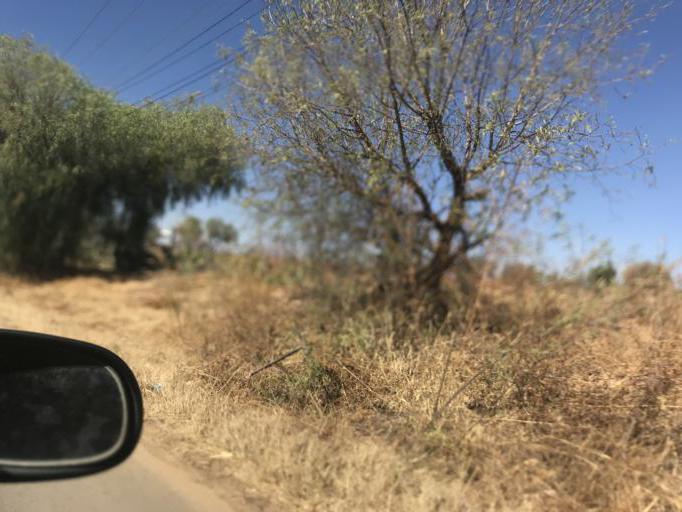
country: BO
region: Cochabamba
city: Tarata
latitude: -17.6074
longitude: -66.0000
